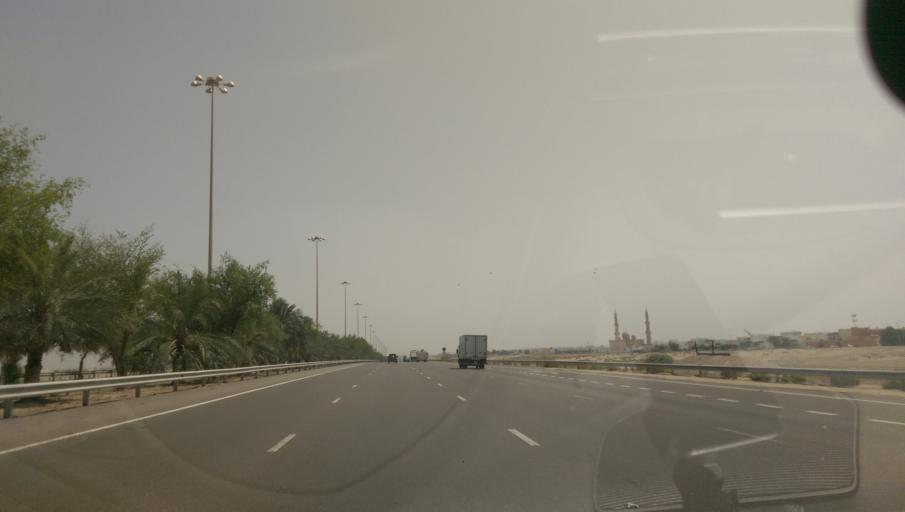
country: AE
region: Abu Dhabi
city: Abu Dhabi
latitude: 24.3462
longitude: 54.6408
